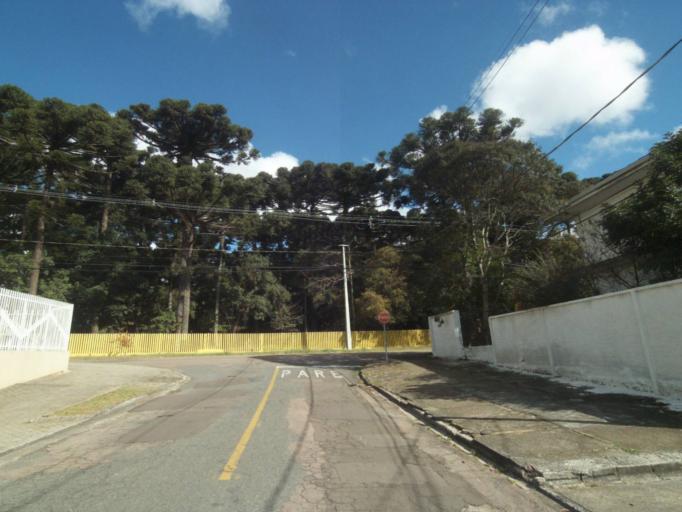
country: BR
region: Parana
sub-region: Sao Jose Dos Pinhais
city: Sao Jose dos Pinhais
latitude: -25.5343
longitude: -49.2909
